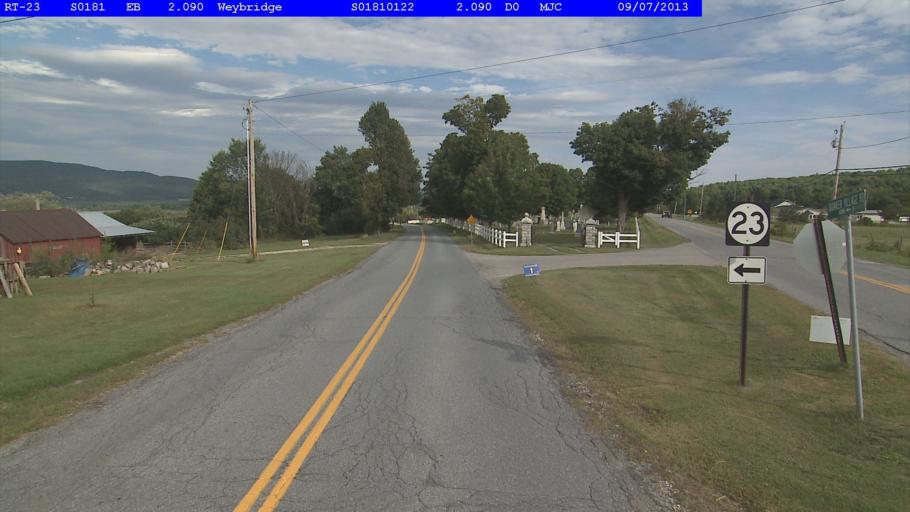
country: US
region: Vermont
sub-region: Addison County
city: Middlebury (village)
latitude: 44.0391
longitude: -73.2129
